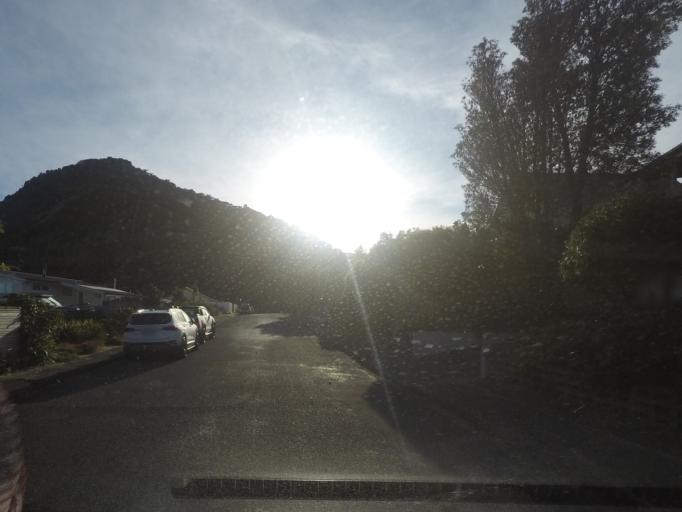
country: NZ
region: Tasman
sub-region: Tasman District
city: Takaka
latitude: -40.8102
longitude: 172.9167
